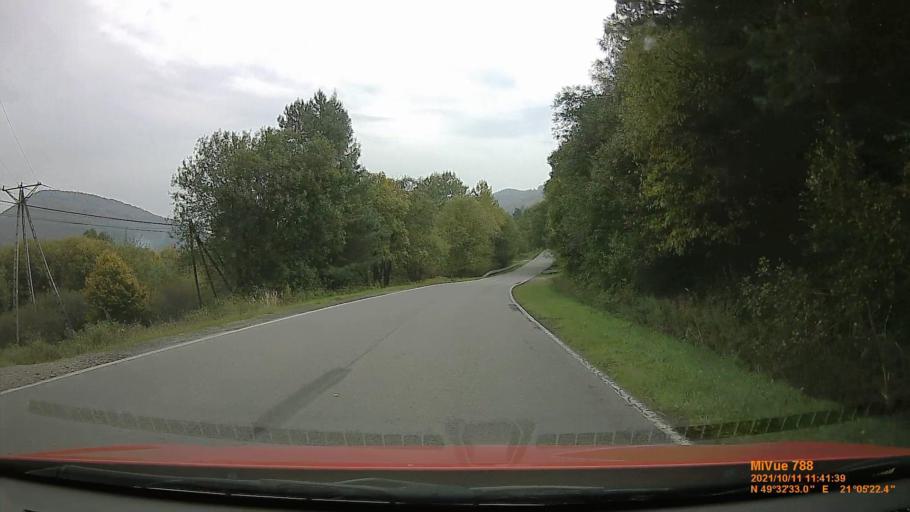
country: PL
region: Lesser Poland Voivodeship
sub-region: Powiat gorlicki
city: Uscie Gorlickie
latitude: 49.5424
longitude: 21.0897
